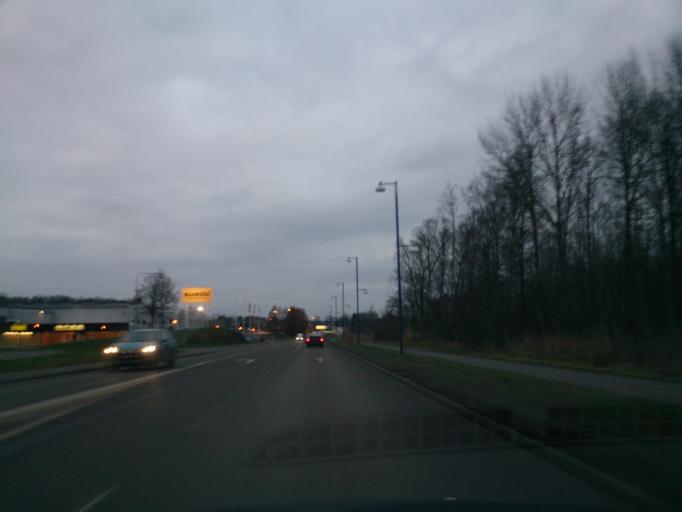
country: SE
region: OEstergoetland
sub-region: Norrkopings Kommun
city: Norrkoping
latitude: 58.6114
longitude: 16.1782
